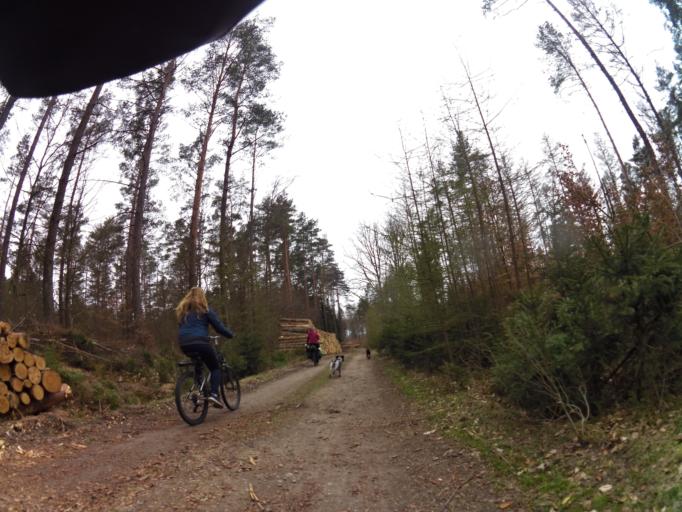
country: PL
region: West Pomeranian Voivodeship
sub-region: Powiat szczecinecki
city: Bialy Bor
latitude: 53.9387
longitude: 16.7185
